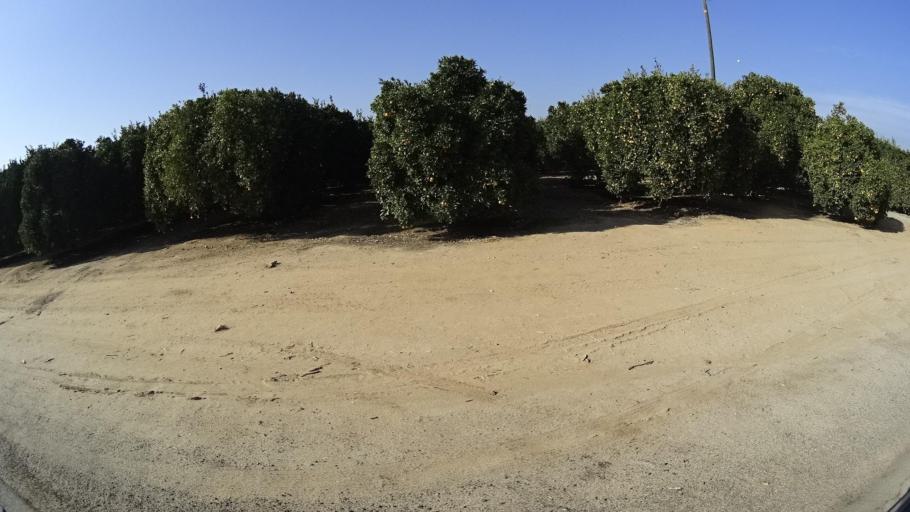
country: US
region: California
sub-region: Kern County
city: McFarland
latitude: 35.6118
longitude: -119.1688
